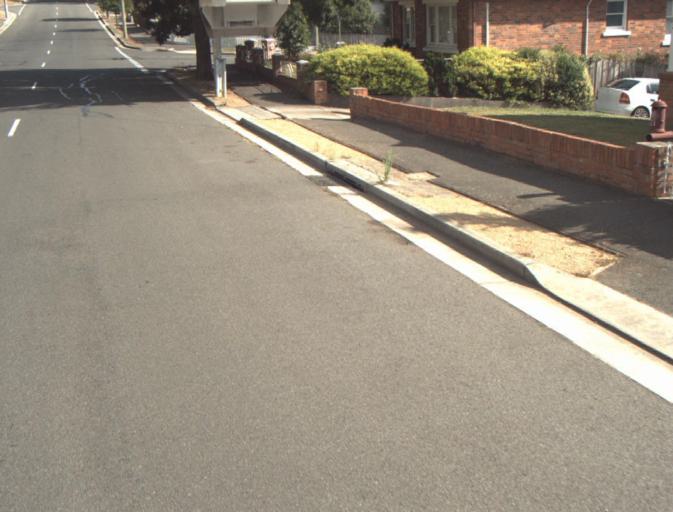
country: AU
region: Tasmania
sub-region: Launceston
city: East Launceston
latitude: -41.4495
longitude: 147.1592
